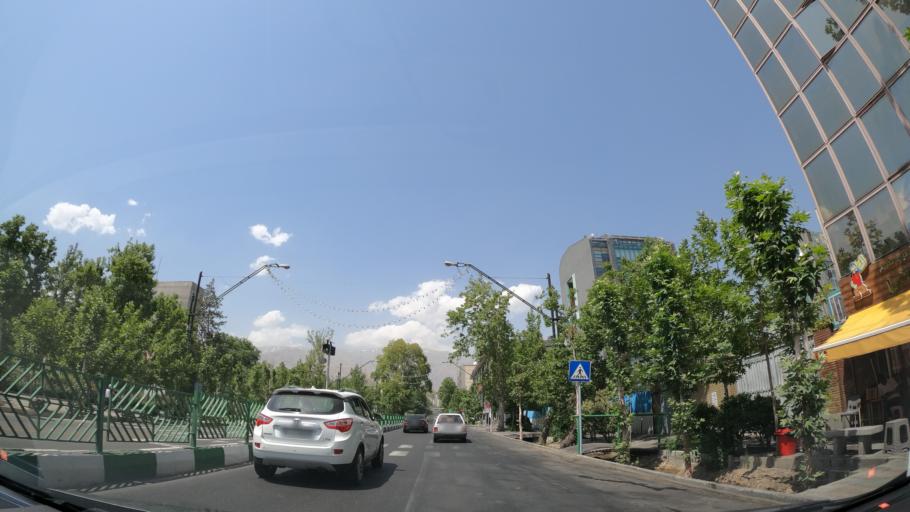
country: IR
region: Tehran
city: Tajrish
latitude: 35.7786
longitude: 51.4136
